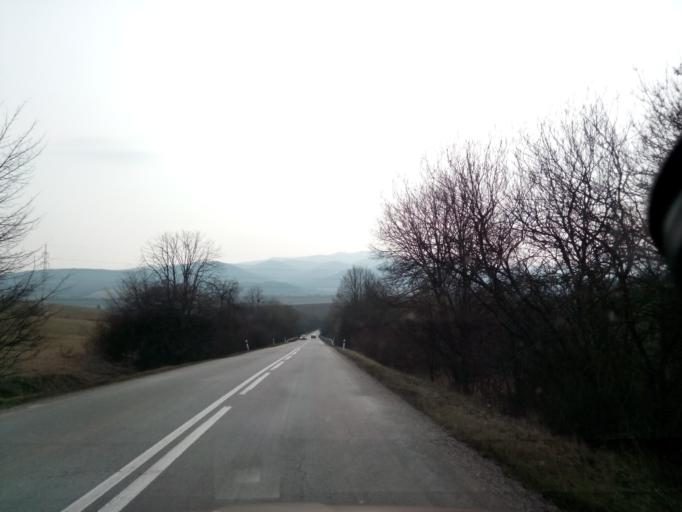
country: SK
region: Kosicky
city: Secovce
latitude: 48.6261
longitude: 21.5526
